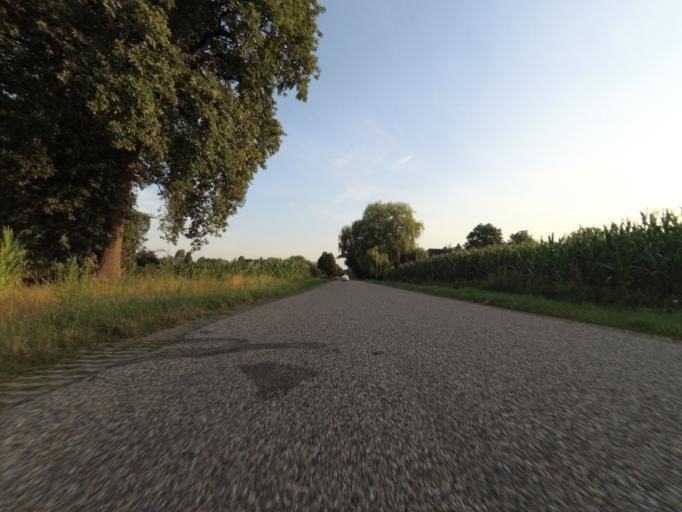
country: NL
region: Overijssel
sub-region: Gemeente Hof van Twente
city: Markelo
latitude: 52.3247
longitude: 6.5068
